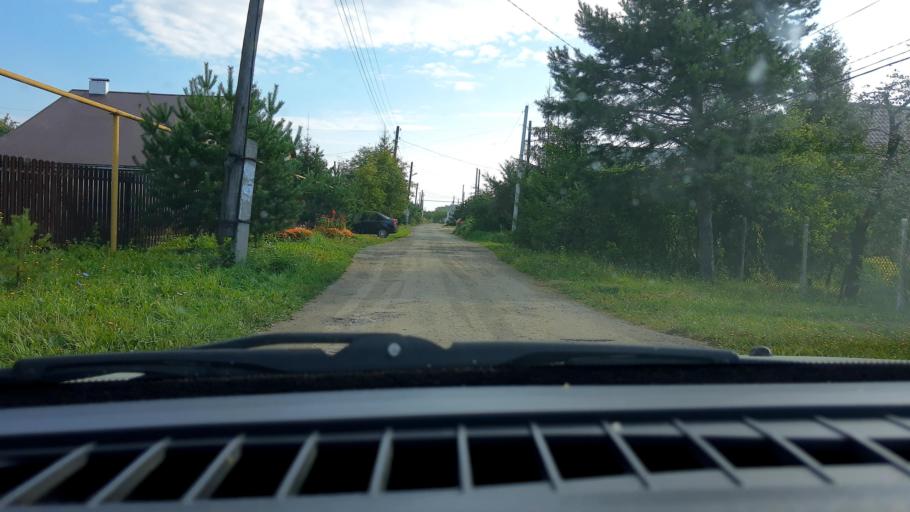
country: RU
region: Nizjnij Novgorod
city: Burevestnik
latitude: 56.1653
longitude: 43.7341
